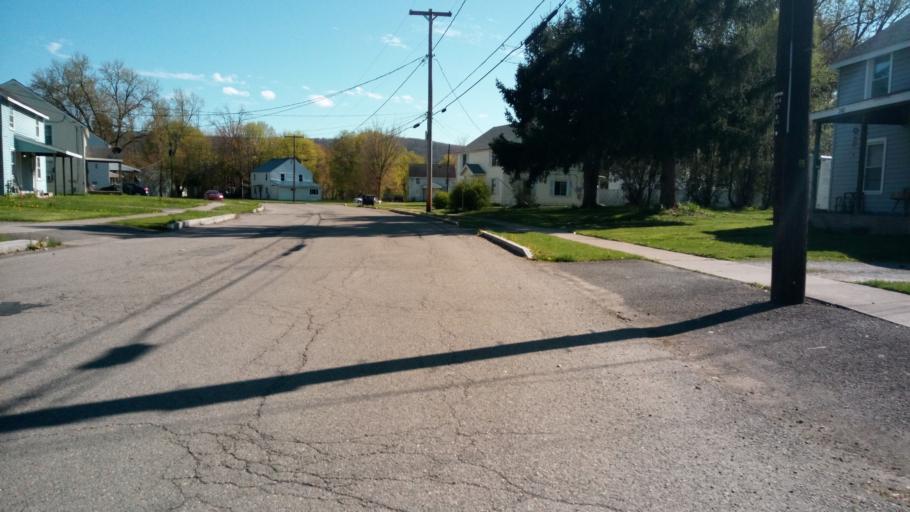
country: US
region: New York
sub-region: Chemung County
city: Southport
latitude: 42.0670
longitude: -76.8014
